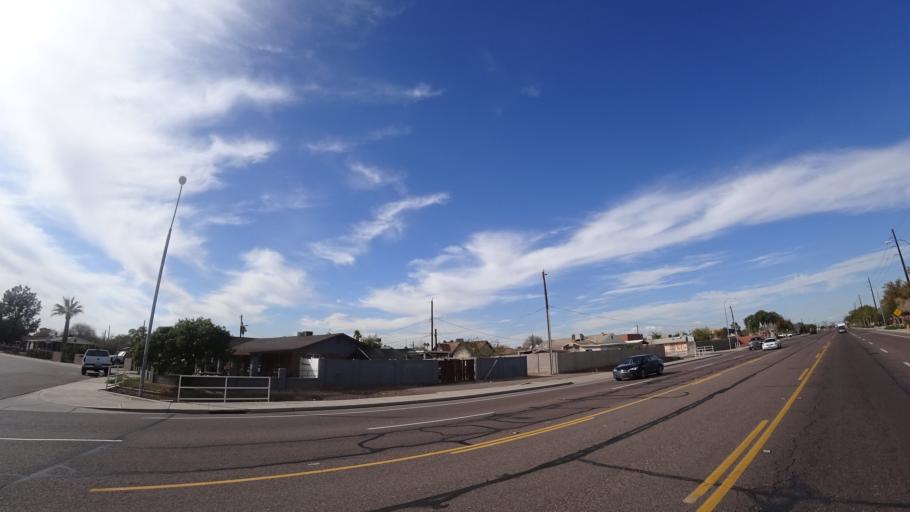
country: US
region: Arizona
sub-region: Maricopa County
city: Tolleson
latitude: 33.4296
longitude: -112.2896
